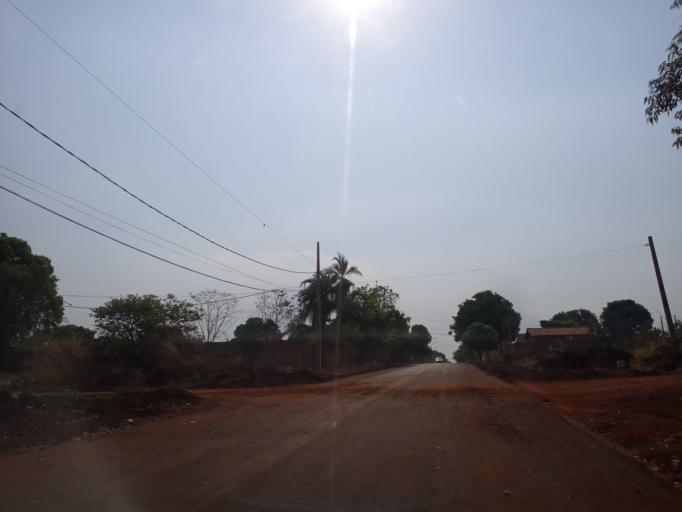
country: BR
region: Minas Gerais
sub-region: Ituiutaba
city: Ituiutaba
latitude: -18.9598
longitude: -49.4769
